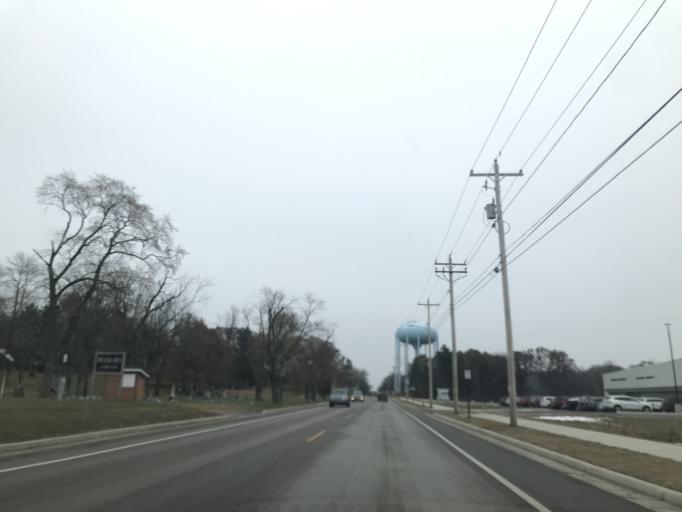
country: US
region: Wisconsin
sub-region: Marinette County
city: Marinette
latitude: 45.0810
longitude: -87.6296
